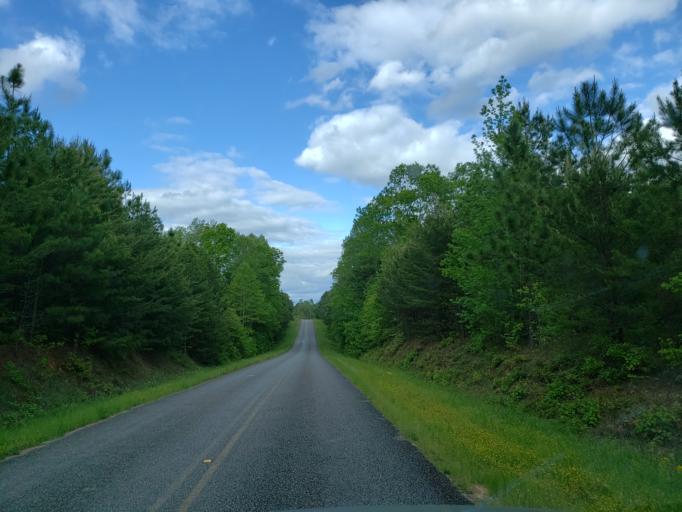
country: US
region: Georgia
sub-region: Haralson County
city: Tallapoosa
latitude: 33.8179
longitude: -85.3808
